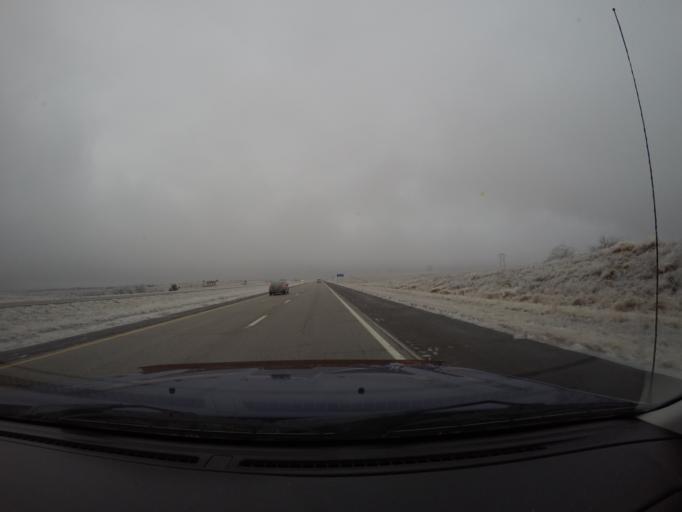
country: US
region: Kansas
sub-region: Riley County
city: Manhattan
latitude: 39.1302
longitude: -96.5380
